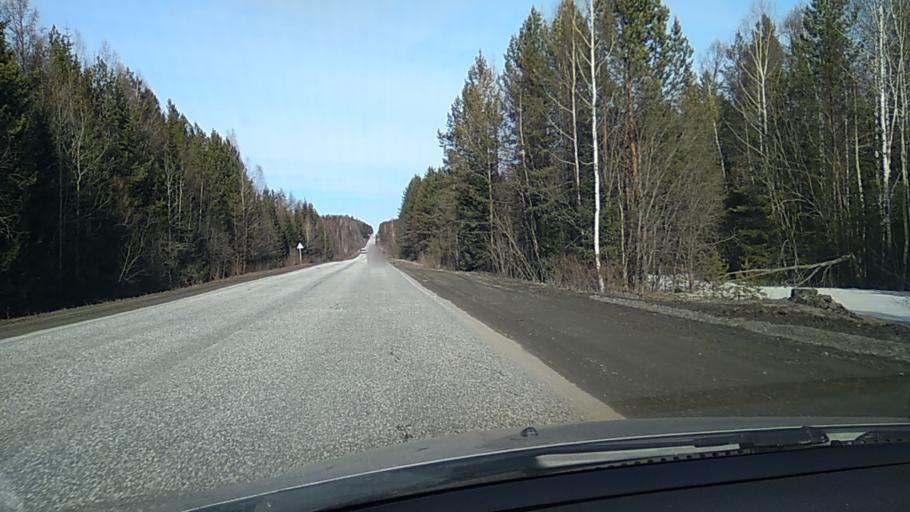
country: RU
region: Sverdlovsk
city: Chernoistochinsk
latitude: 57.7843
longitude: 59.8987
